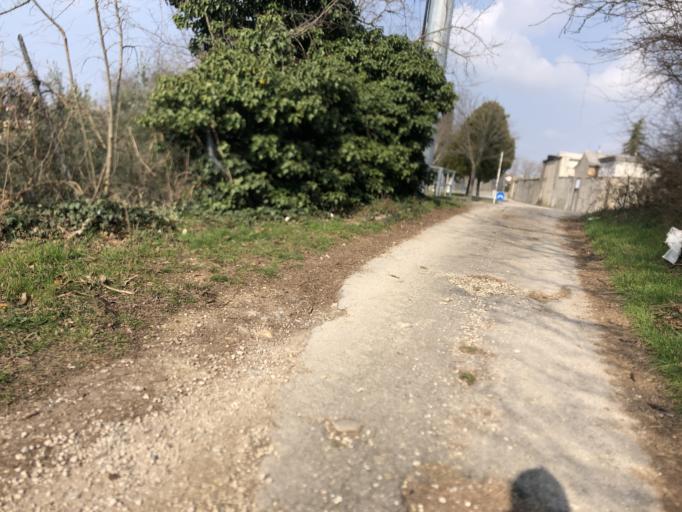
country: IT
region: Veneto
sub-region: Provincia di Verona
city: Sona
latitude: 45.4299
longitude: 10.8363
